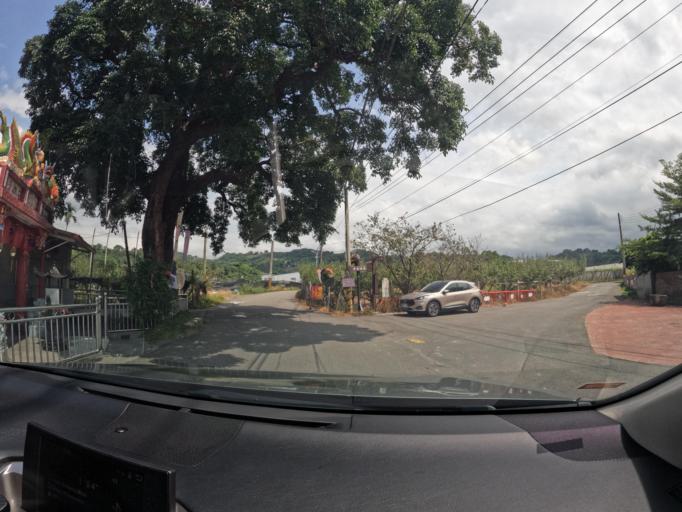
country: TW
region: Taiwan
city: Fengyuan
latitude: 24.3083
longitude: 120.8329
